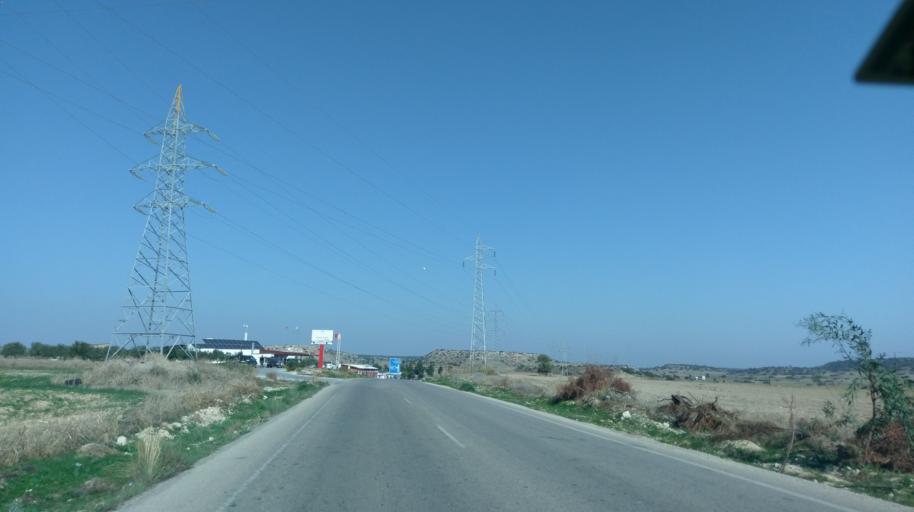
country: CY
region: Ammochostos
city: Leonarisso
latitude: 35.3796
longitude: 34.0390
